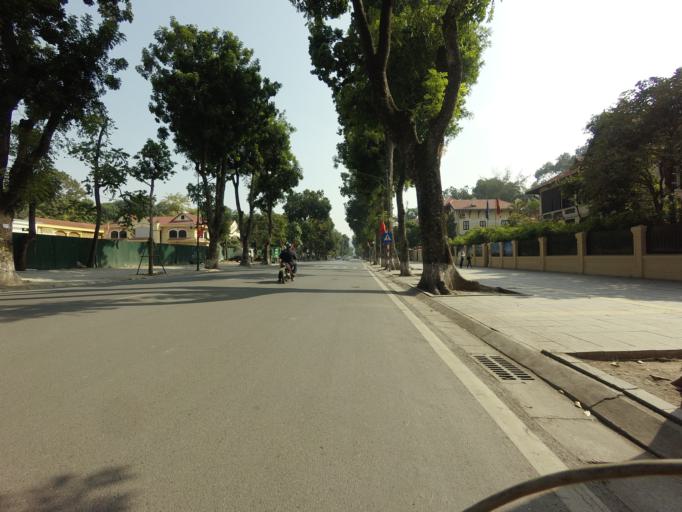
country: VN
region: Ha Noi
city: Hanoi
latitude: 21.0345
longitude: 105.8373
